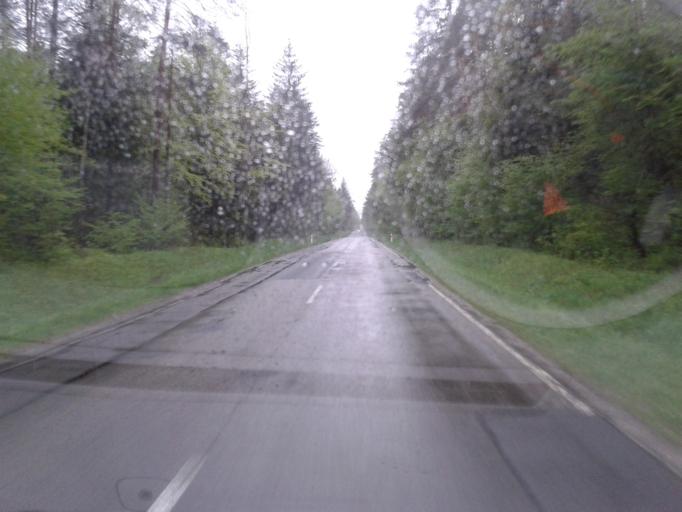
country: PL
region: Subcarpathian Voivodeship
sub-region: Powiat lubaczowski
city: Nowe Siolo
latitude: 50.2997
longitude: 23.2158
